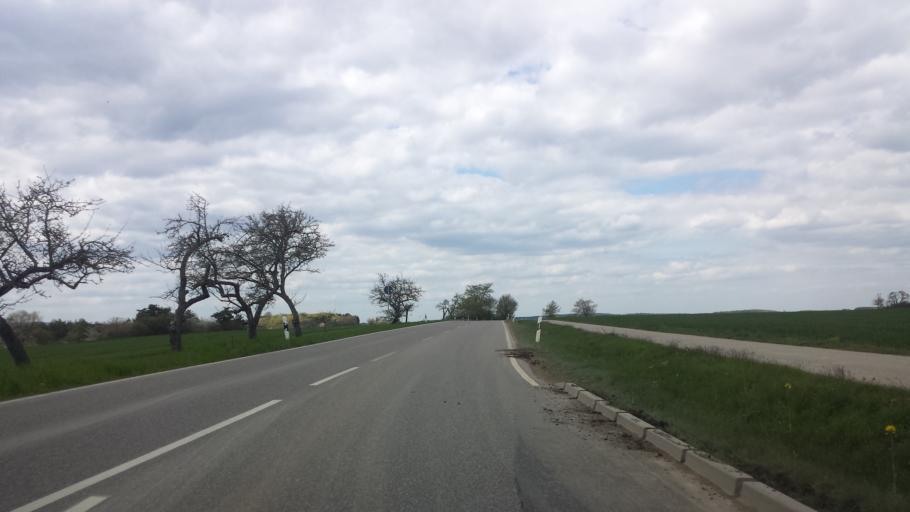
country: DE
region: Baden-Wuerttemberg
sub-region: Regierungsbezirk Stuttgart
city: Weissach
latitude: 48.8546
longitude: 8.8977
